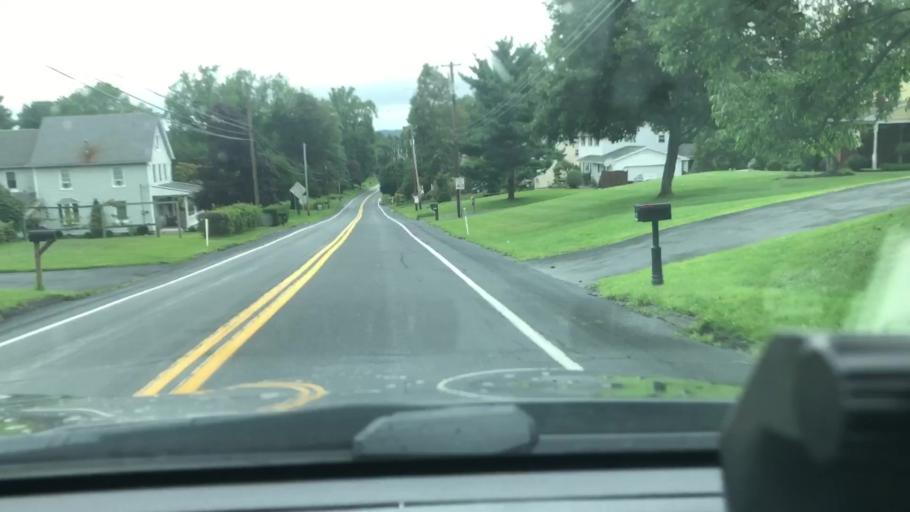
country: US
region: Pennsylvania
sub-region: Lehigh County
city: Coopersburg
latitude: 40.4993
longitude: -75.3931
